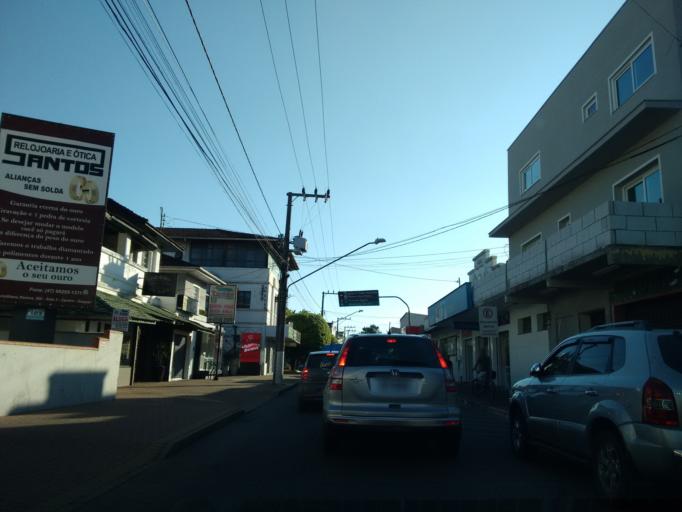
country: BR
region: Santa Catarina
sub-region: Gaspar
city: Gaspar
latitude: -26.9286
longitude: -48.9555
